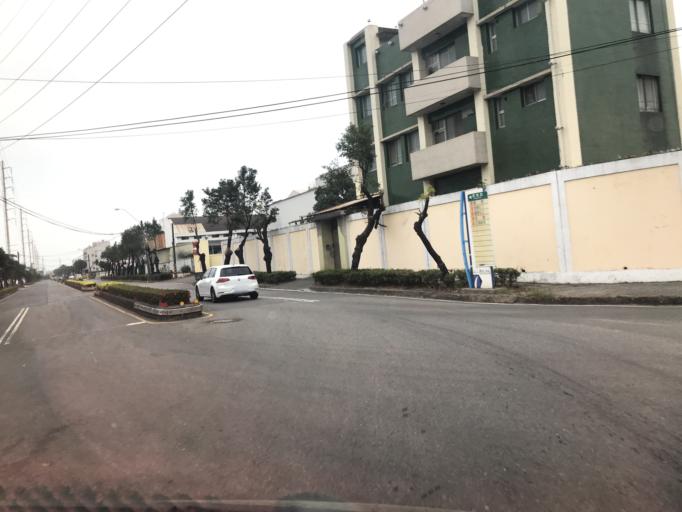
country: TW
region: Taiwan
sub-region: Pingtung
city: Pingtung
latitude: 22.4121
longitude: 120.5770
